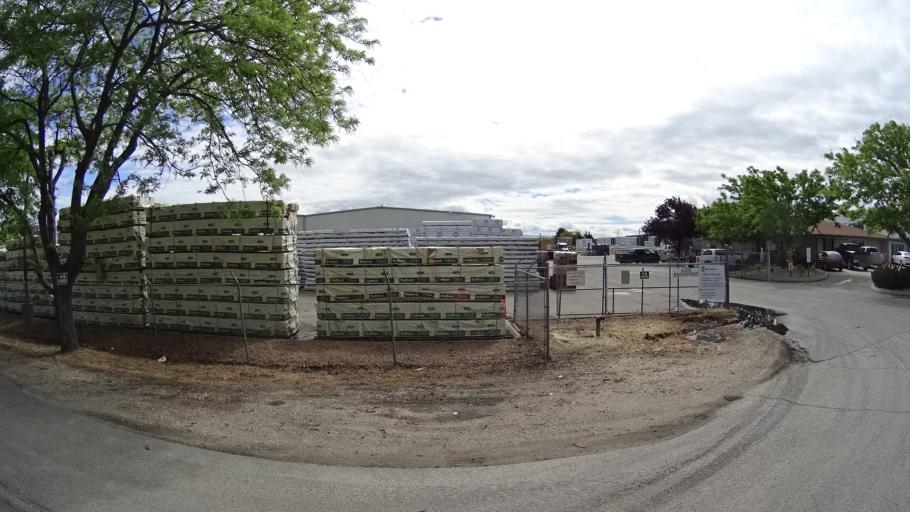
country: US
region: Idaho
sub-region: Ada County
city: Boise
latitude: 43.5636
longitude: -116.1987
